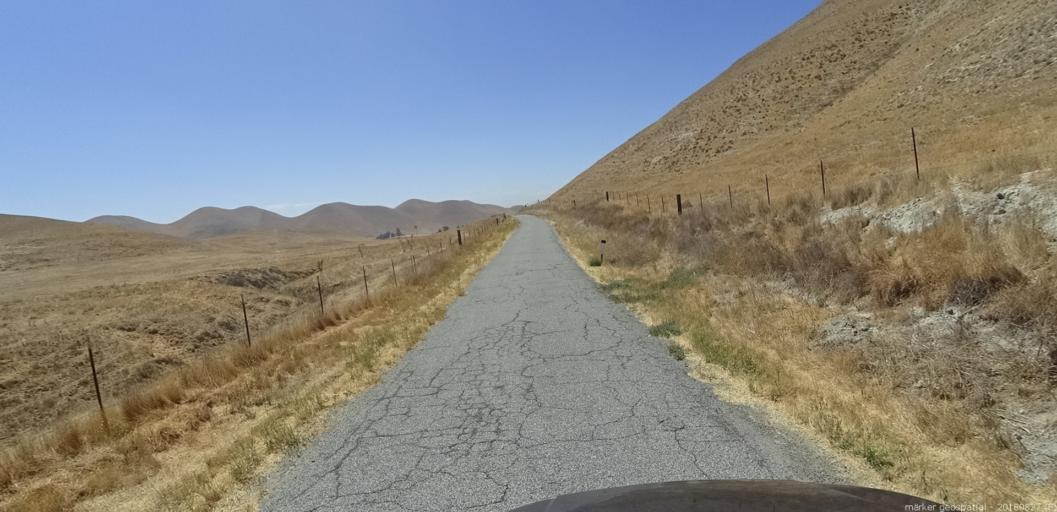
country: US
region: California
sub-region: Monterey County
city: King City
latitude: 36.1097
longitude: -120.8763
